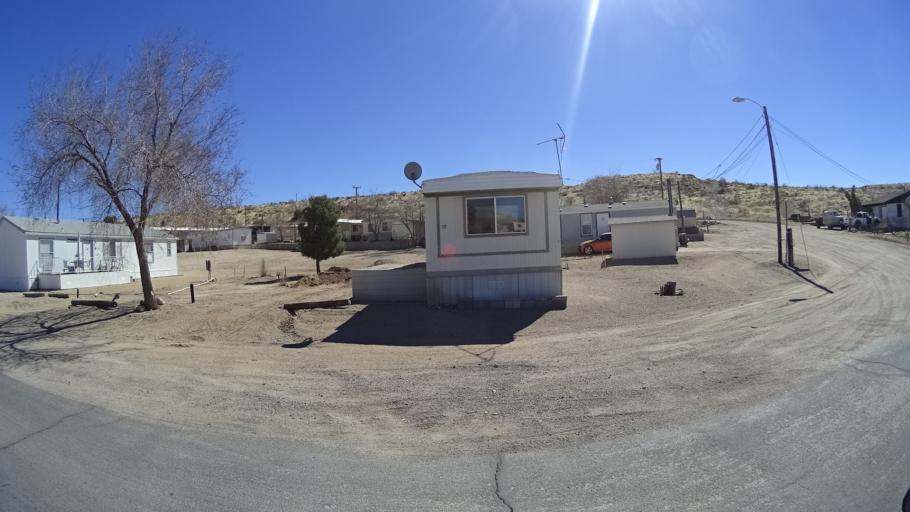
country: US
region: Arizona
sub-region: Mohave County
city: Kingman
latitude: 35.1842
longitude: -114.0549
